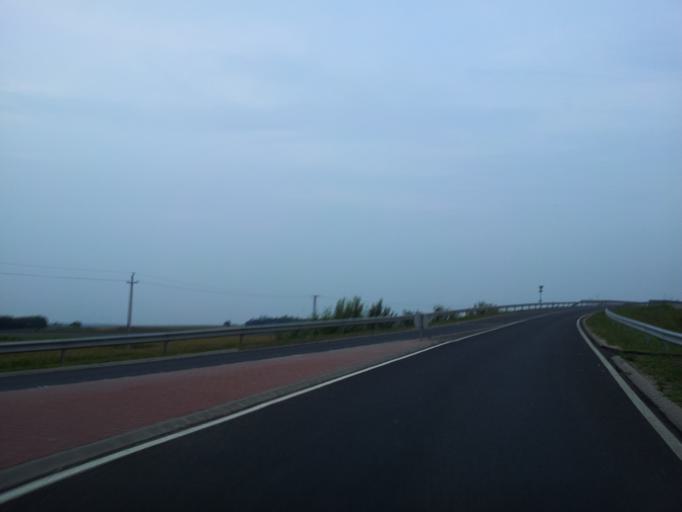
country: HU
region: Tolna
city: Tolna
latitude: 46.4097
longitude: 18.7359
